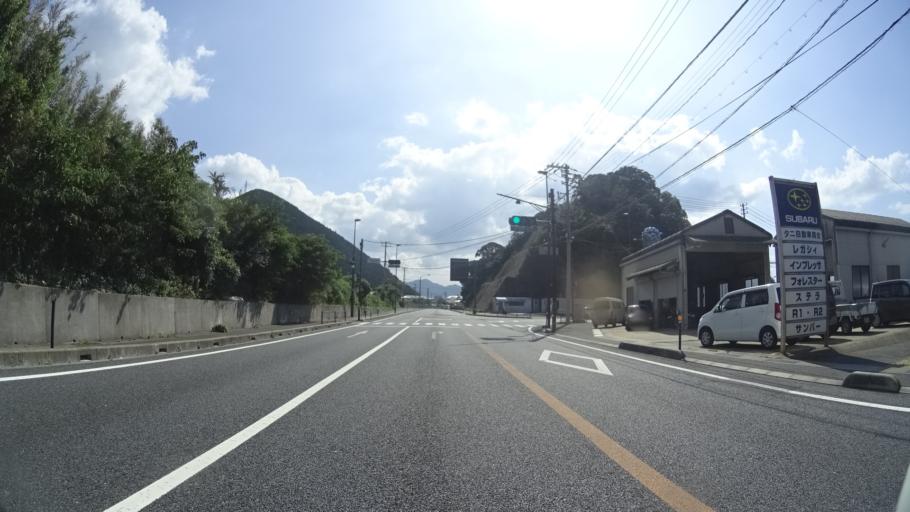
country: JP
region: Yamaguchi
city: Hagi
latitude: 34.4261
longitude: 131.4168
